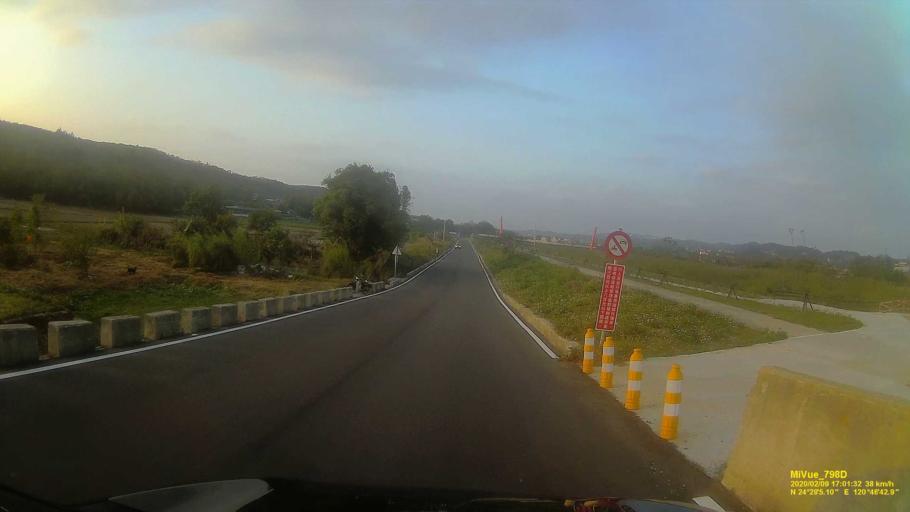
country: TW
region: Taiwan
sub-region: Miaoli
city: Miaoli
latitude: 24.4849
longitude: 120.7786
